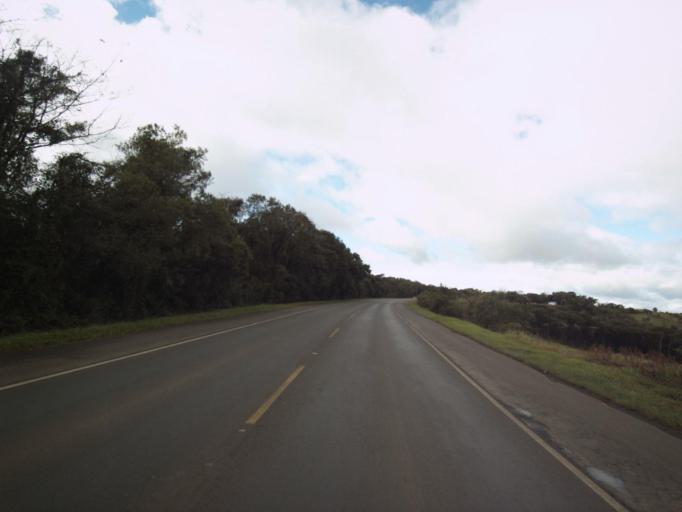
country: BR
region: Santa Catarina
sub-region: Concordia
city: Concordia
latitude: -27.0944
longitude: -51.9021
